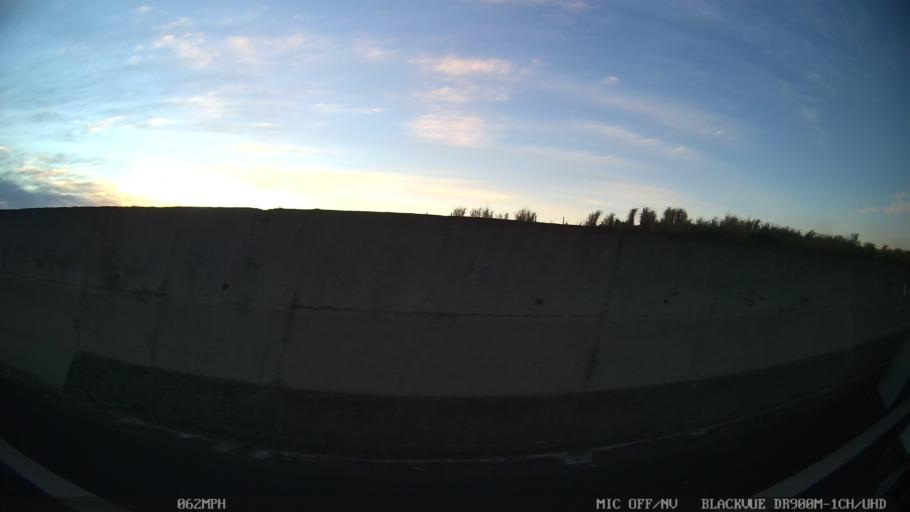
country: BR
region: Sao Paulo
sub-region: Catanduva
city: Catanduva
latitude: -21.1148
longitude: -48.9765
